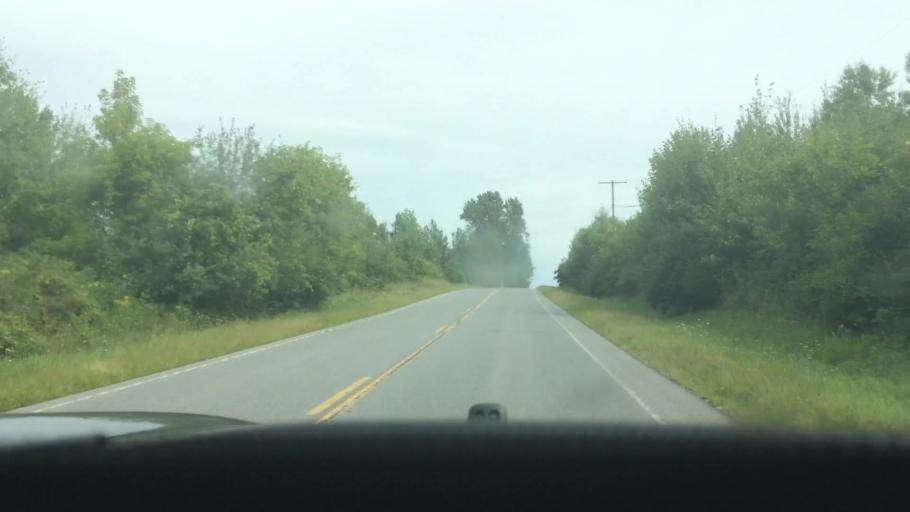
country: US
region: New York
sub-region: St. Lawrence County
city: Canton
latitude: 44.4817
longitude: -75.2228
